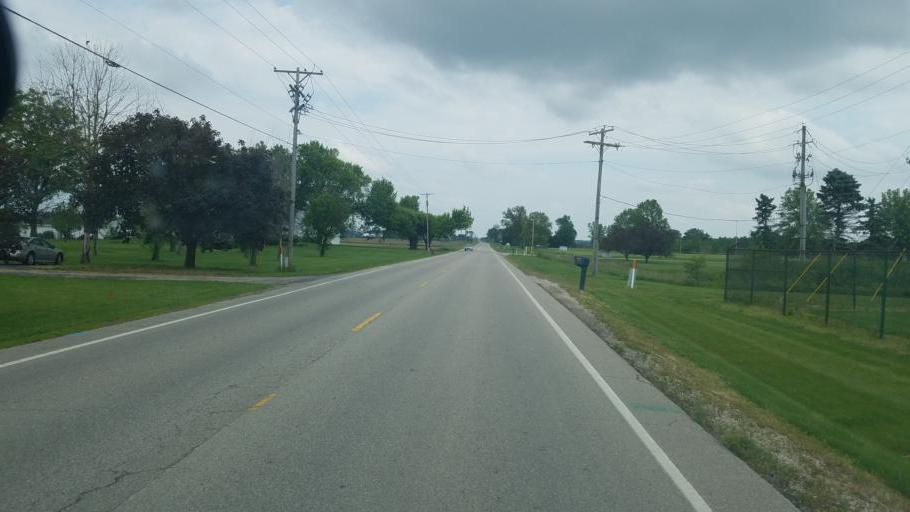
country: US
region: Ohio
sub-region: Union County
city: Marysville
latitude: 40.2006
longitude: -83.3044
